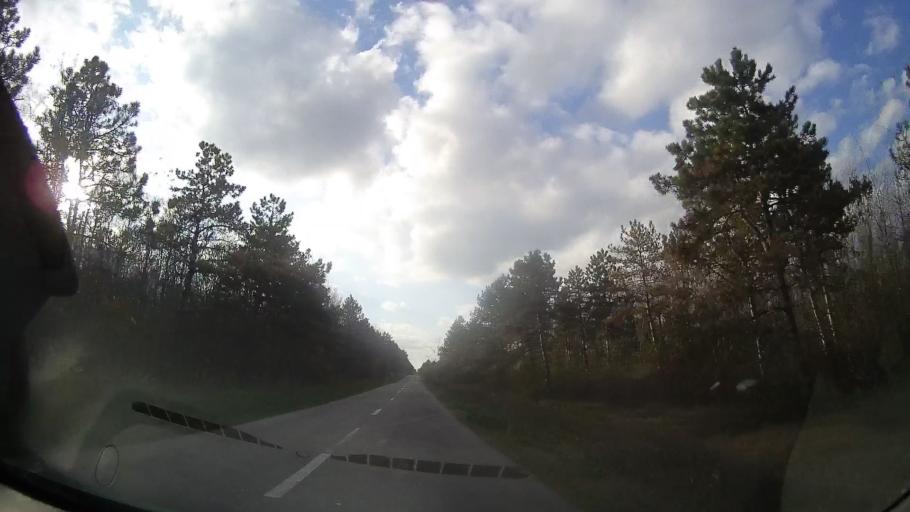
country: RO
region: Constanta
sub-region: Comuna Negru Voda
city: Negru Voda
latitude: 43.8193
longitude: 28.2684
